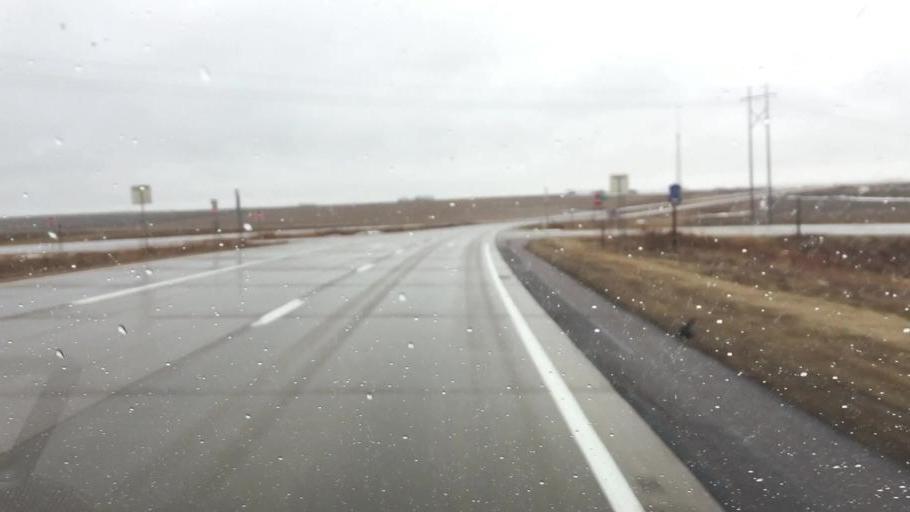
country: US
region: Iowa
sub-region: O'Brien County
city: Sheldon
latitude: 43.0627
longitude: -95.9006
